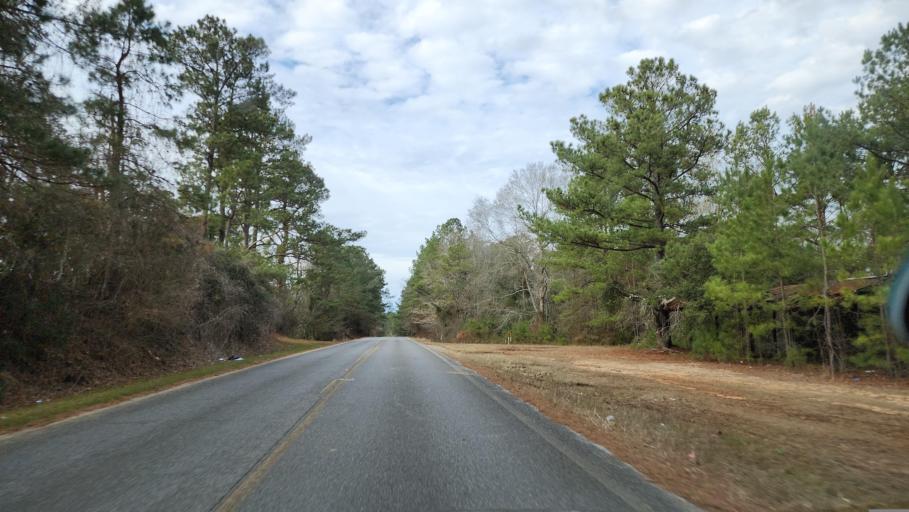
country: US
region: Mississippi
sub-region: Clarke County
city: Stonewall
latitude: 32.1945
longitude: -88.6822
